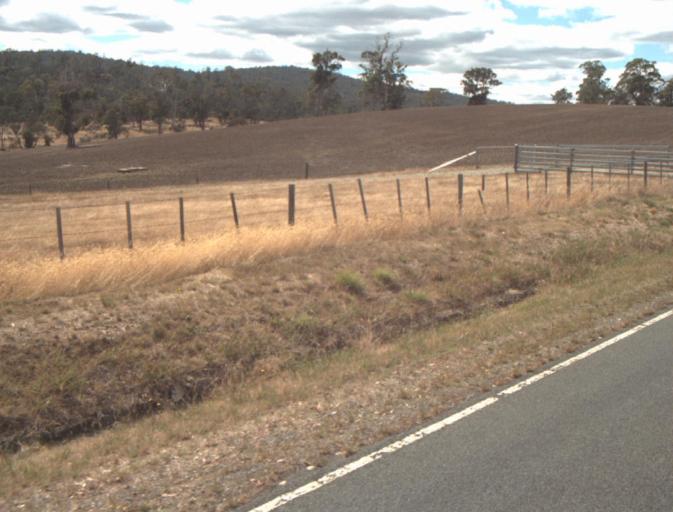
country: AU
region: Tasmania
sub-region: Launceston
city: Mayfield
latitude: -41.3343
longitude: 147.0776
